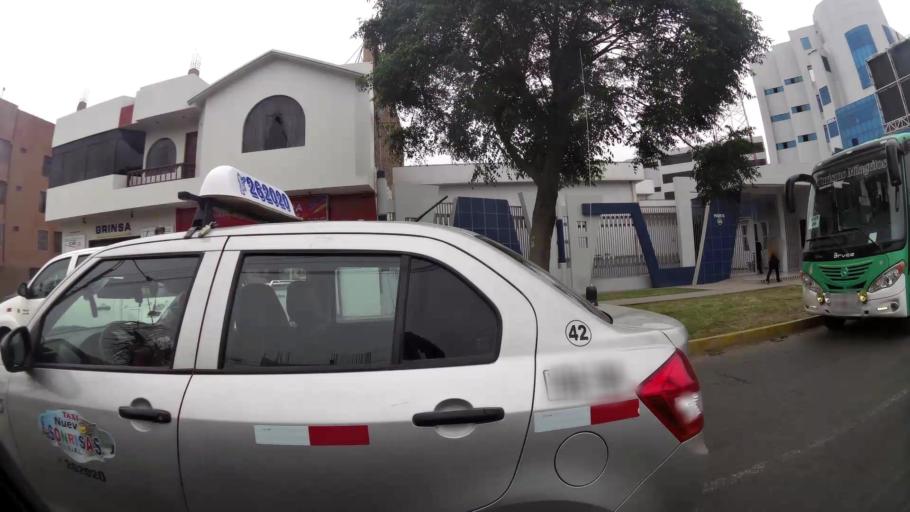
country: PE
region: La Libertad
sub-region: Provincia de Trujillo
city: Buenos Aires
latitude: -8.1305
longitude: -79.0440
